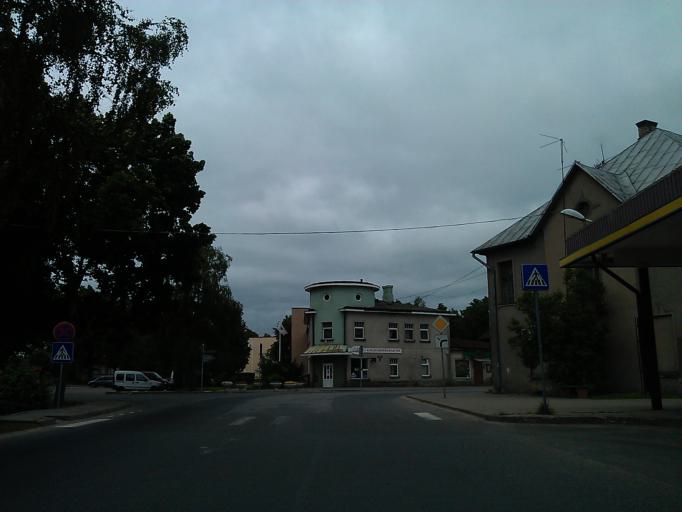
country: LV
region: Carnikava
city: Carnikava
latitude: 57.1293
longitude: 24.2792
